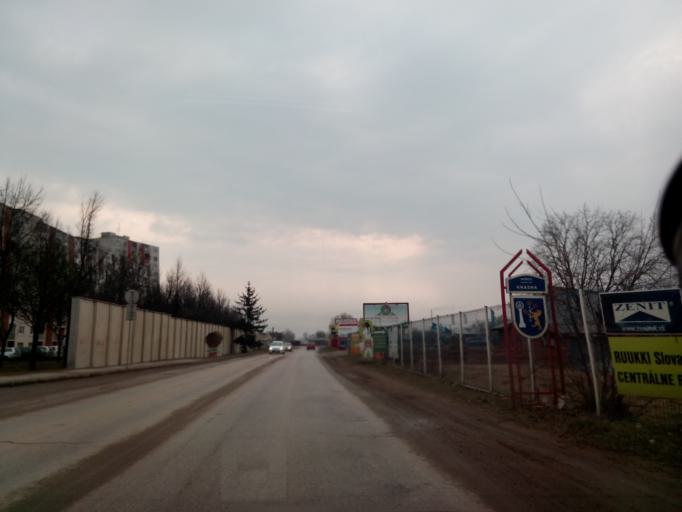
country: SK
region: Kosicky
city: Kosice
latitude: 48.6736
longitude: 21.3019
